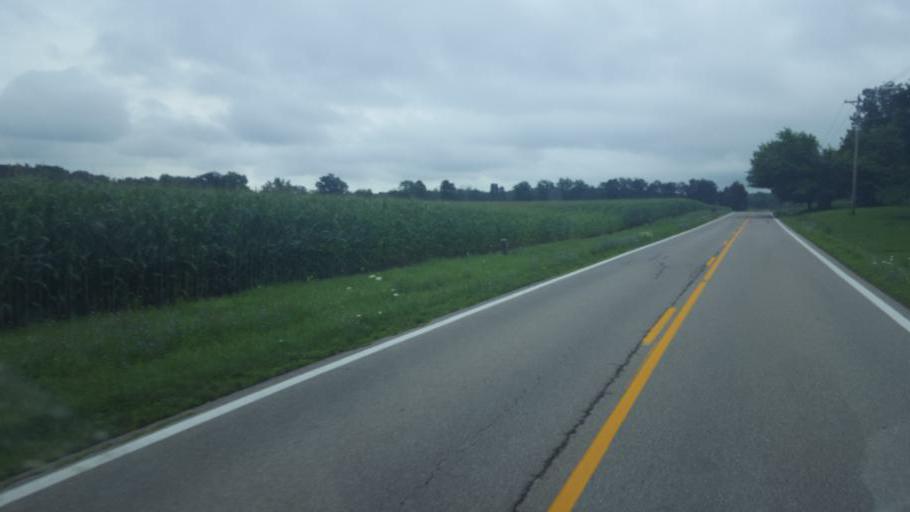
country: US
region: Ohio
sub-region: Delaware County
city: Sunbury
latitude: 40.3215
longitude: -82.8524
